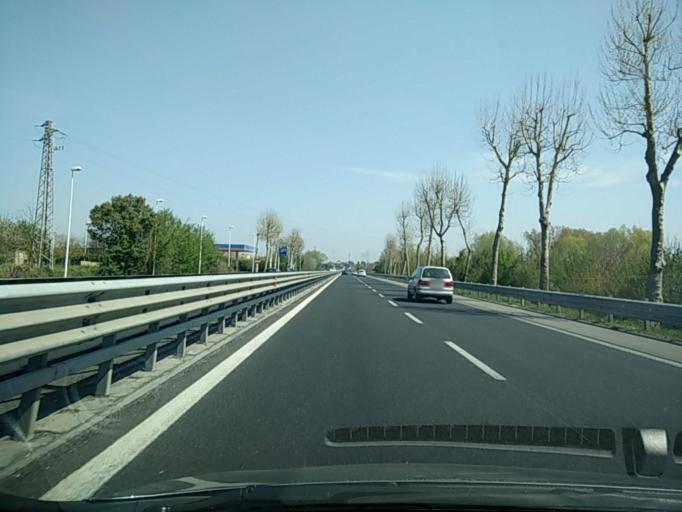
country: IT
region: Veneto
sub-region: Provincia di Treviso
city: Casier
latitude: 45.6550
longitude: 12.2716
